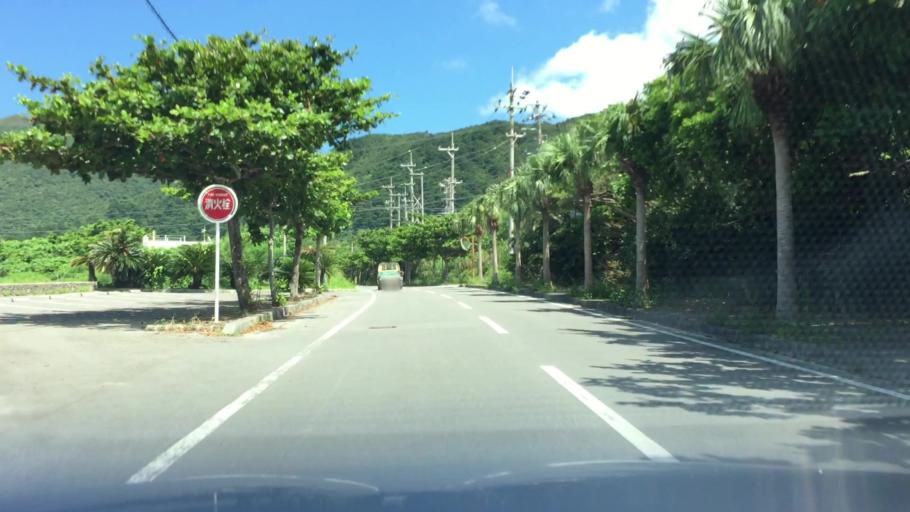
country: JP
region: Okinawa
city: Ishigaki
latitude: 24.4470
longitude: 124.1706
